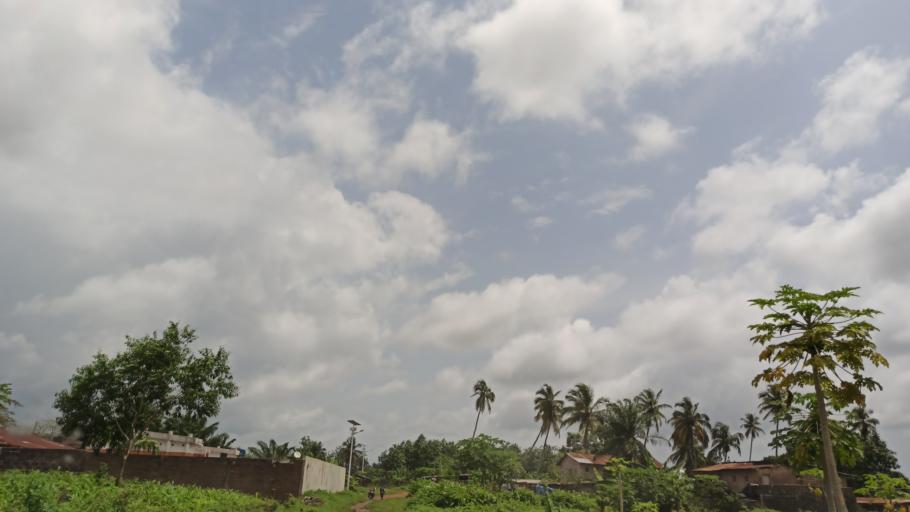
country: BJ
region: Queme
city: Porto-Novo
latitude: 6.4674
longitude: 2.6307
